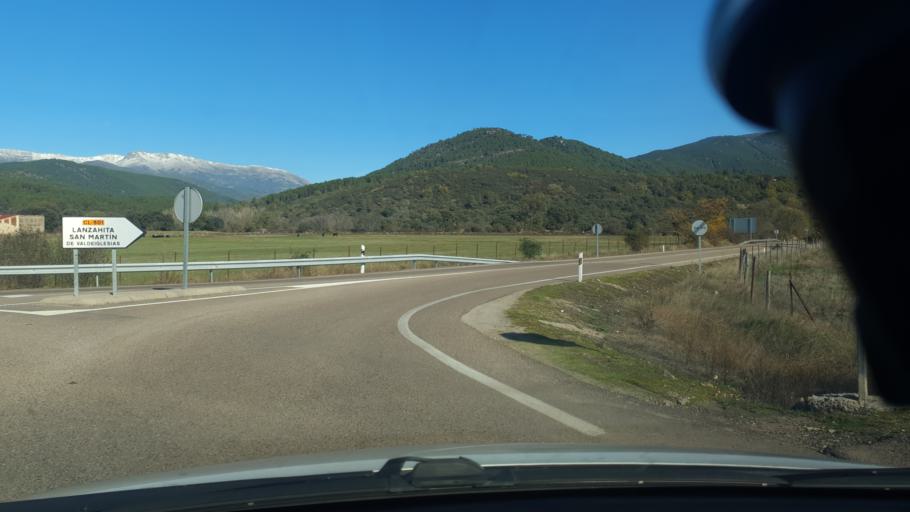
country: ES
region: Castille and Leon
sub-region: Provincia de Avila
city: Arenas de San Pedro
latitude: 40.1796
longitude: -5.0402
